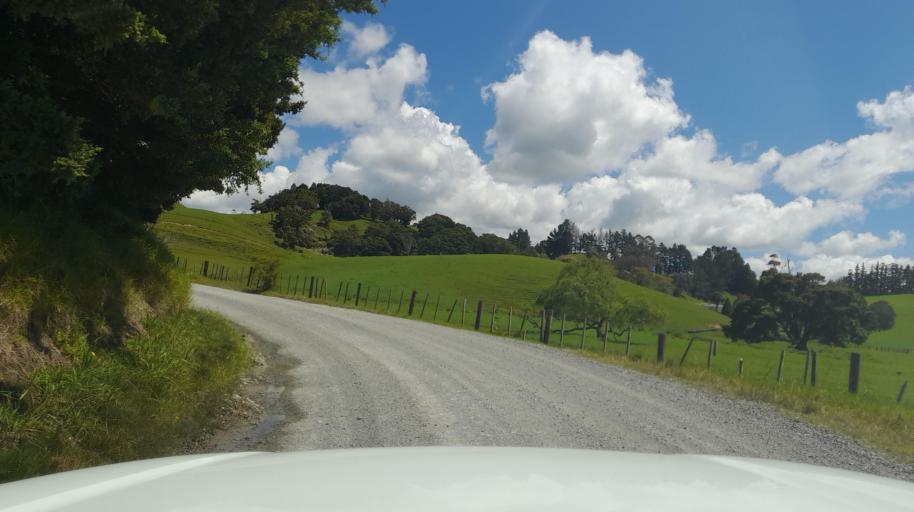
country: NZ
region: Northland
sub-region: Far North District
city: Kaitaia
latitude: -35.1167
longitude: 173.3941
